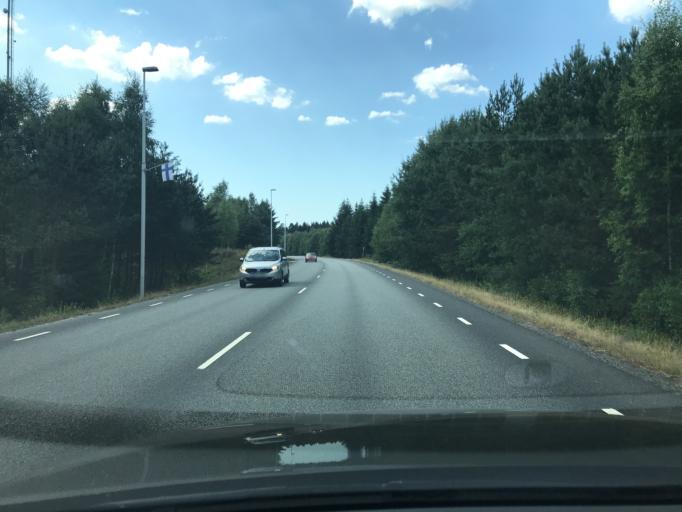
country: SE
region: Skane
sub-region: Hassleholms Kommun
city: Hastveda
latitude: 56.2750
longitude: 13.9483
